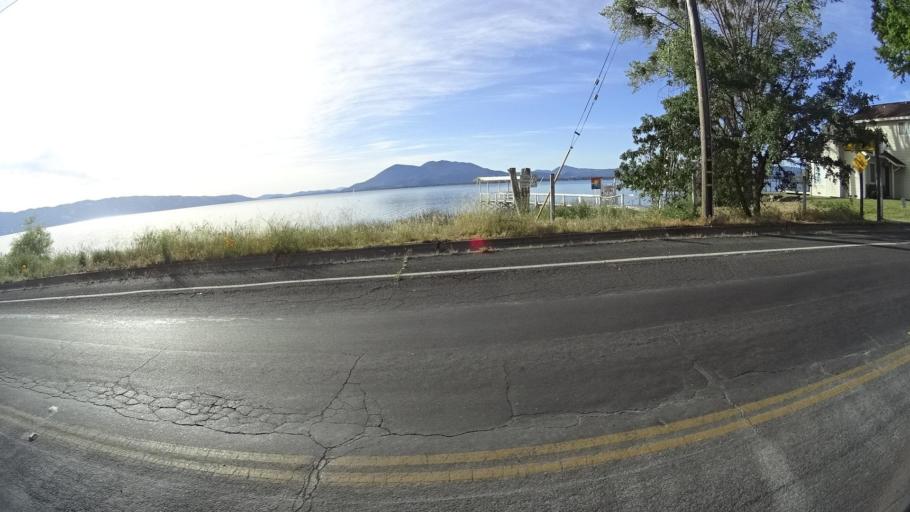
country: US
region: California
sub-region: Lake County
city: Lakeport
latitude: 39.0562
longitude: -122.9135
